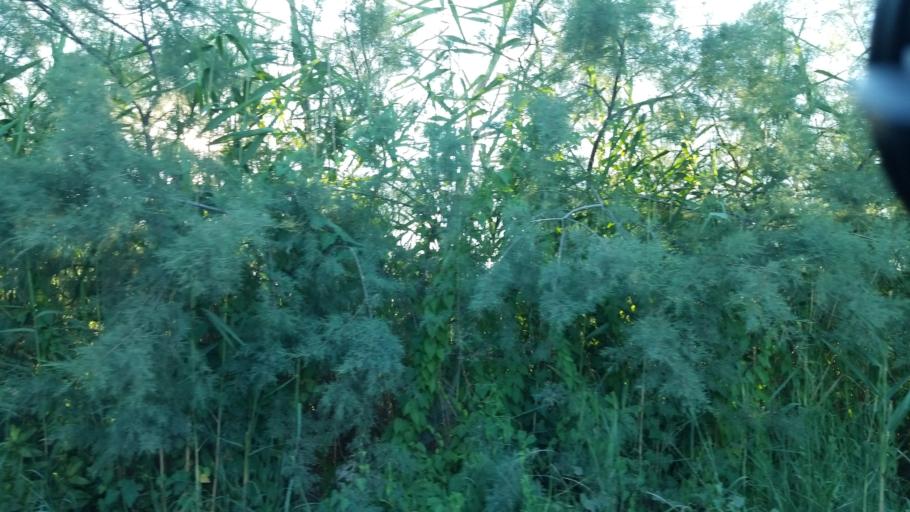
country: AL
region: Shkoder
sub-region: Rrethi i Shkodres
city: Velipoje
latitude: 41.8609
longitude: 19.4397
